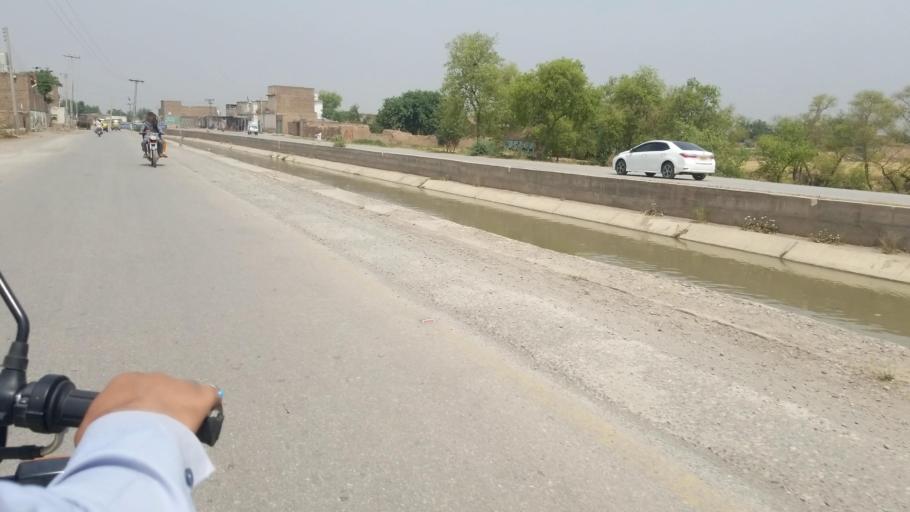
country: PK
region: Khyber Pakhtunkhwa
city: Peshawar
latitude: 33.9548
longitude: 71.5509
